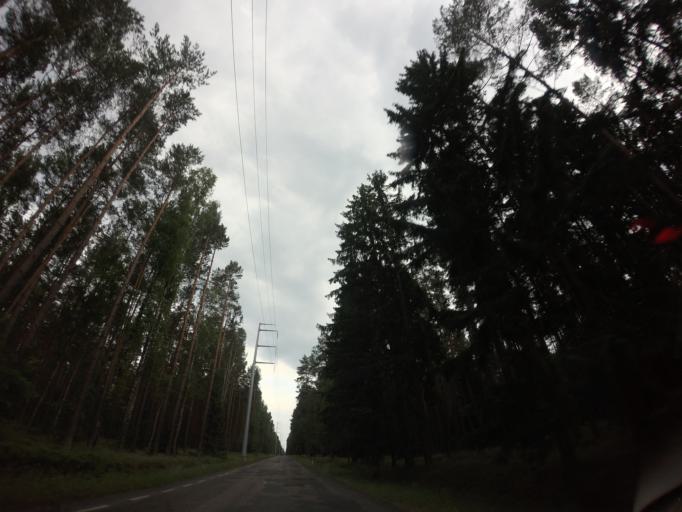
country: PL
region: West Pomeranian Voivodeship
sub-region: Powiat drawski
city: Czaplinek
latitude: 53.4678
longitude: 16.2216
